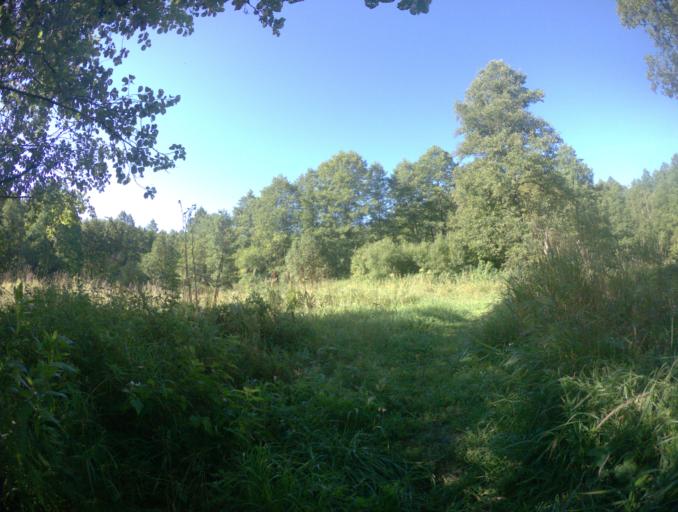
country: RU
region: Vladimir
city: Krasnaya Gorbatka
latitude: 55.7890
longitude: 41.6622
